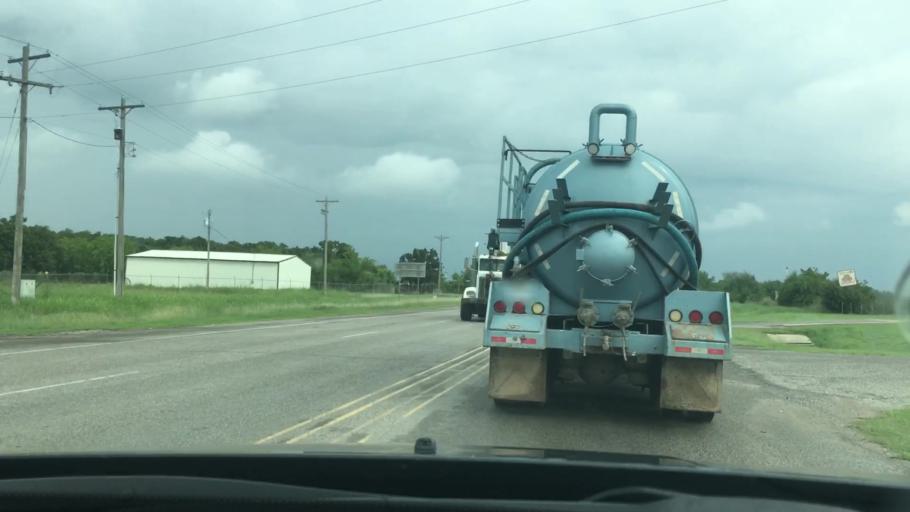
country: US
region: Oklahoma
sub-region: Carter County
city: Wilson
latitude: 34.1739
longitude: -97.4748
